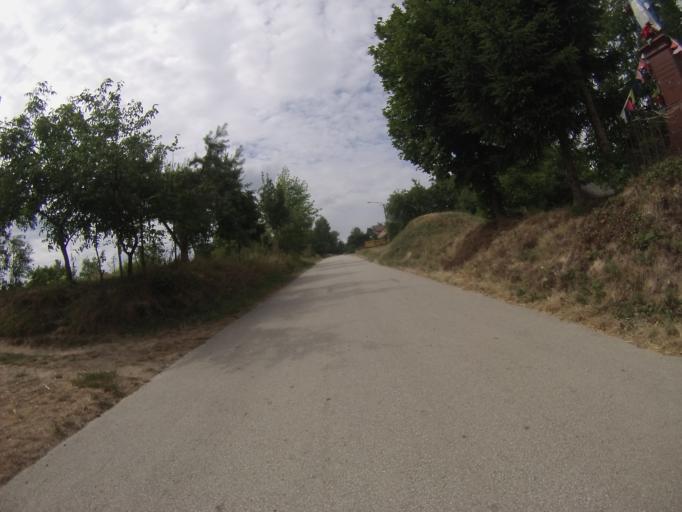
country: PL
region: Swietokrzyskie
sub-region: Powiat kielecki
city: Lagow
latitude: 50.7426
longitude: 21.1059
